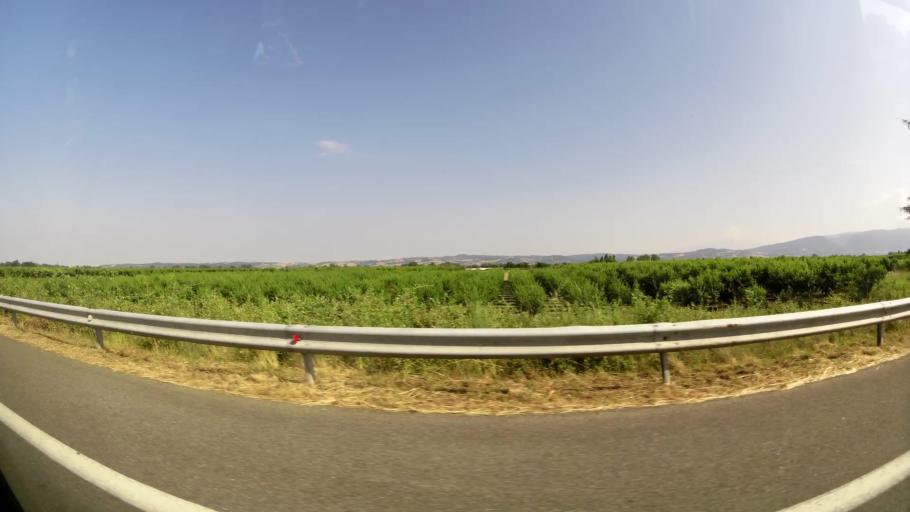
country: GR
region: Central Macedonia
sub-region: Nomos Imathias
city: Loutros
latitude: 40.5685
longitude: 22.3810
